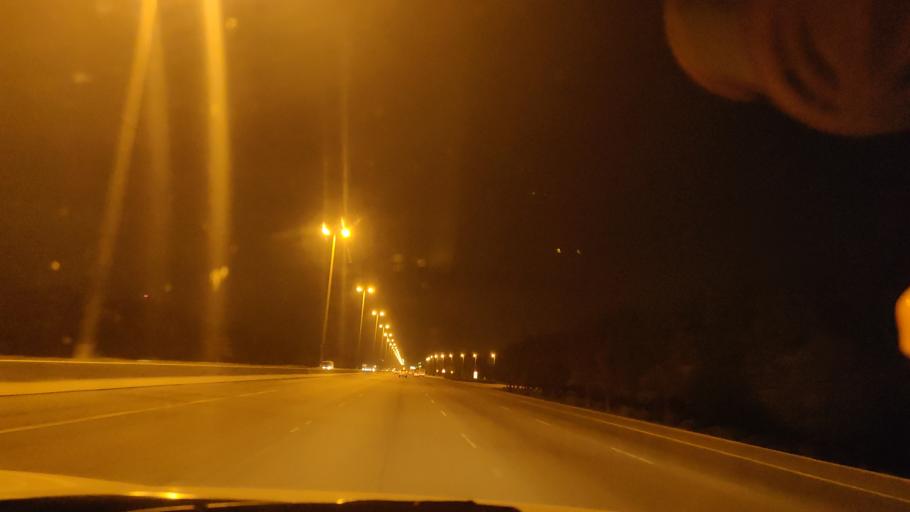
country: KW
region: Mubarak al Kabir
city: Sabah as Salim
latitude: 29.2193
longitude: 48.0560
